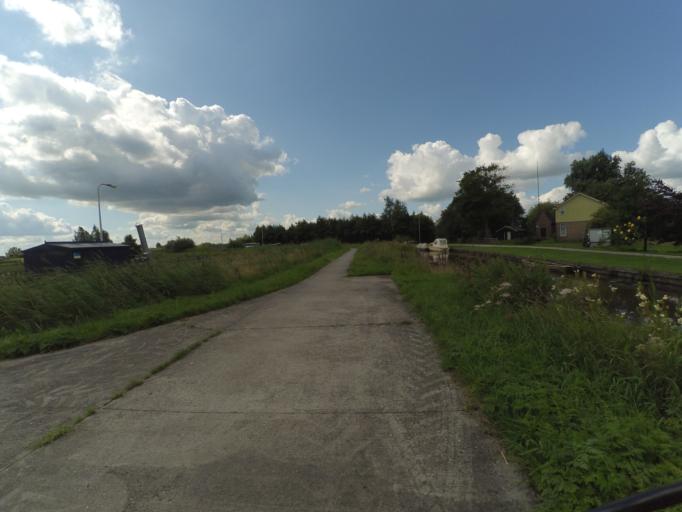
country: NL
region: Friesland
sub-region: Gemeente Tytsjerksteradiel
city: Eastermar
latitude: 53.2070
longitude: 6.0522
